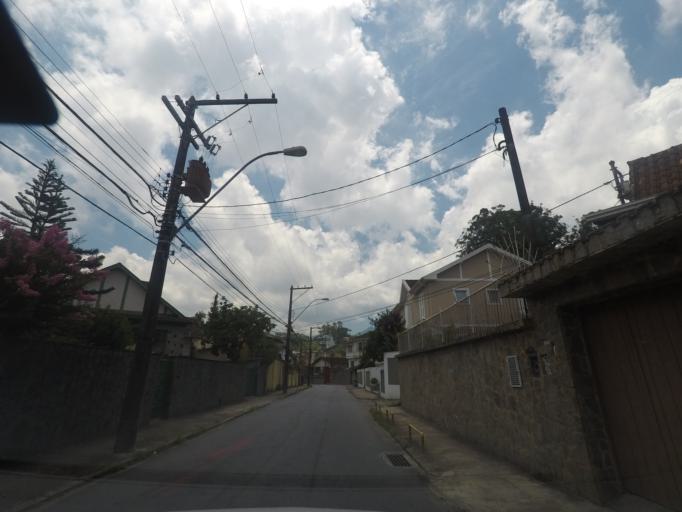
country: BR
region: Rio de Janeiro
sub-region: Petropolis
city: Petropolis
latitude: -22.5211
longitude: -43.1914
